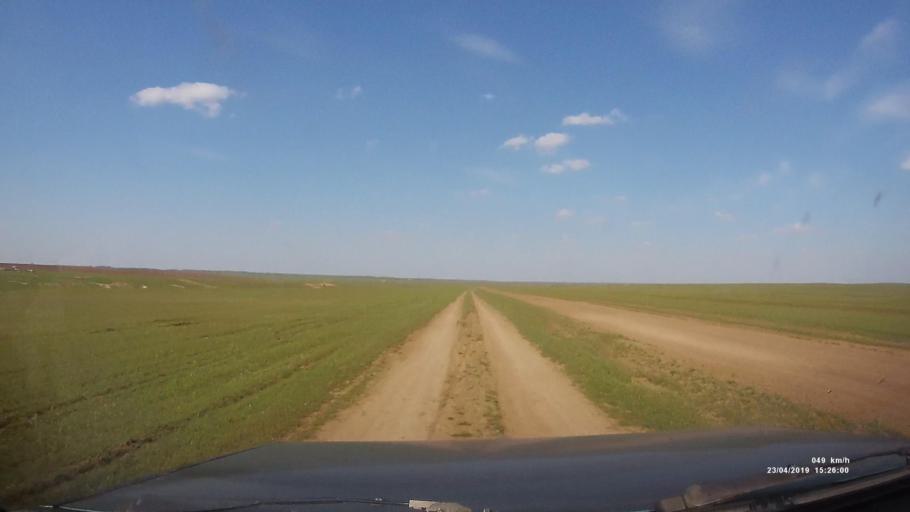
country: RU
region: Rostov
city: Remontnoye
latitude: 46.5438
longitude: 42.9859
